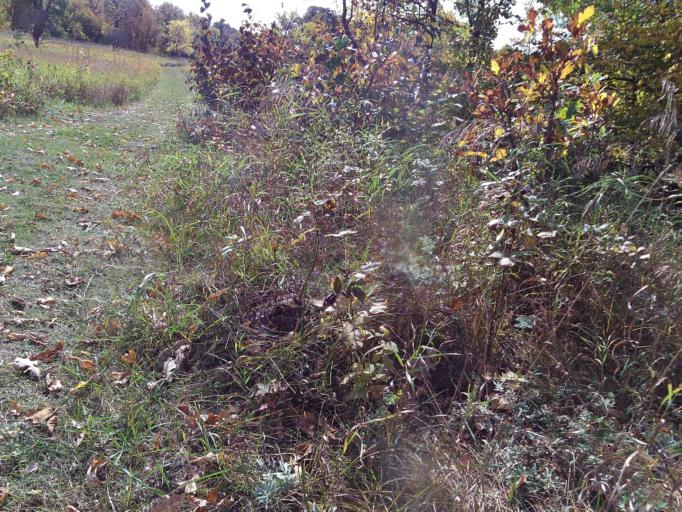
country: US
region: North Dakota
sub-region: Pembina County
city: Cavalier
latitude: 48.7784
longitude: -97.7313
